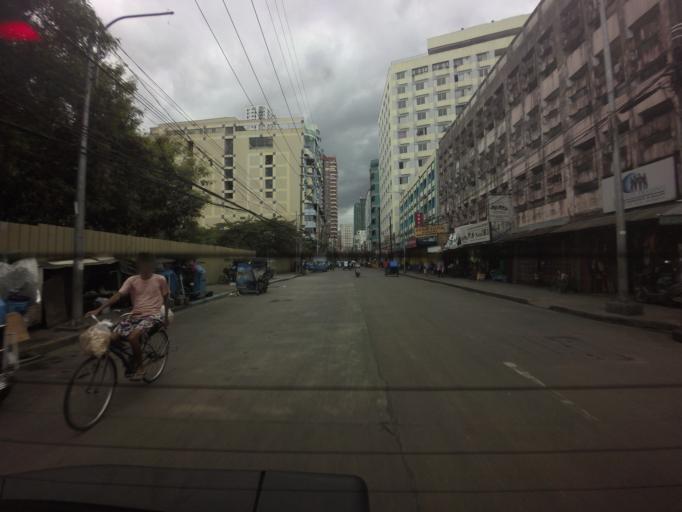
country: PH
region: Metro Manila
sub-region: City of Manila
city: Manila
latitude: 14.6073
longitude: 120.9695
